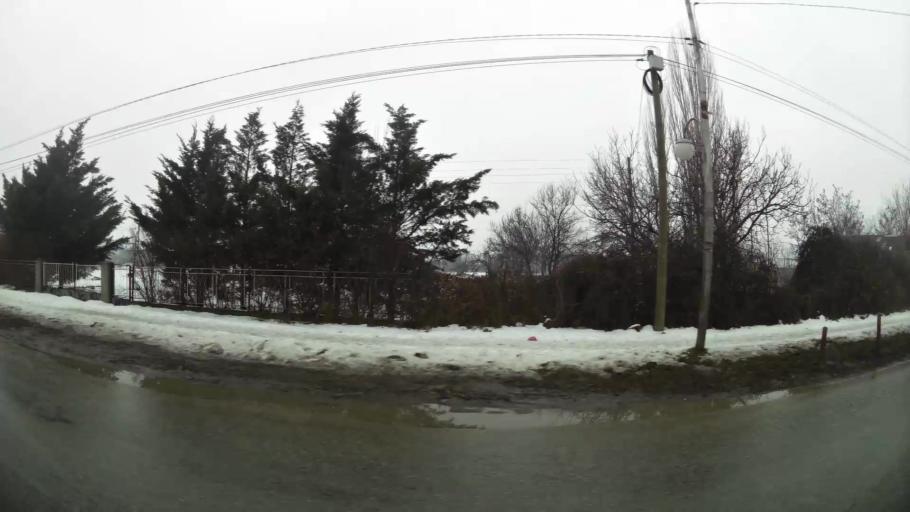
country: MK
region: Petrovec
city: Petrovec
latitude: 41.9282
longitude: 21.6278
